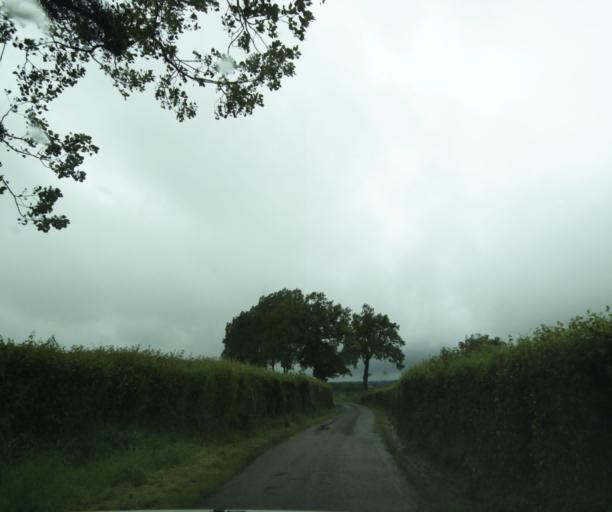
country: FR
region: Bourgogne
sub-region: Departement de Saone-et-Loire
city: Charolles
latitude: 46.3841
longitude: 4.2232
